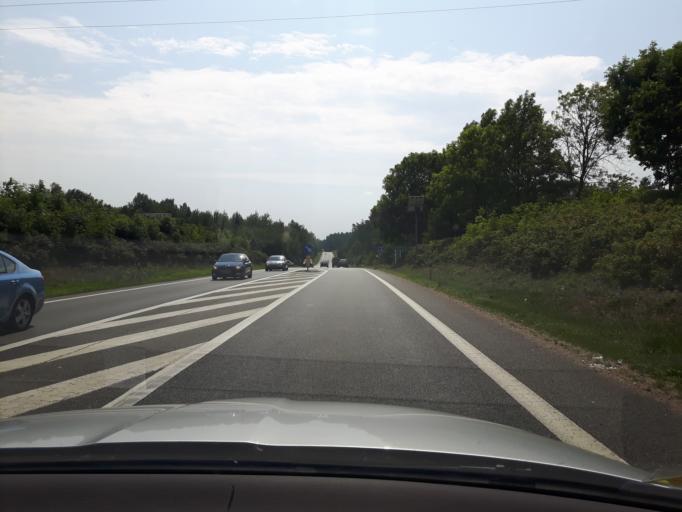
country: PL
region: Masovian Voivodeship
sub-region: Powiat mlawski
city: Mlawa
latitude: 53.1460
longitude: 20.4013
